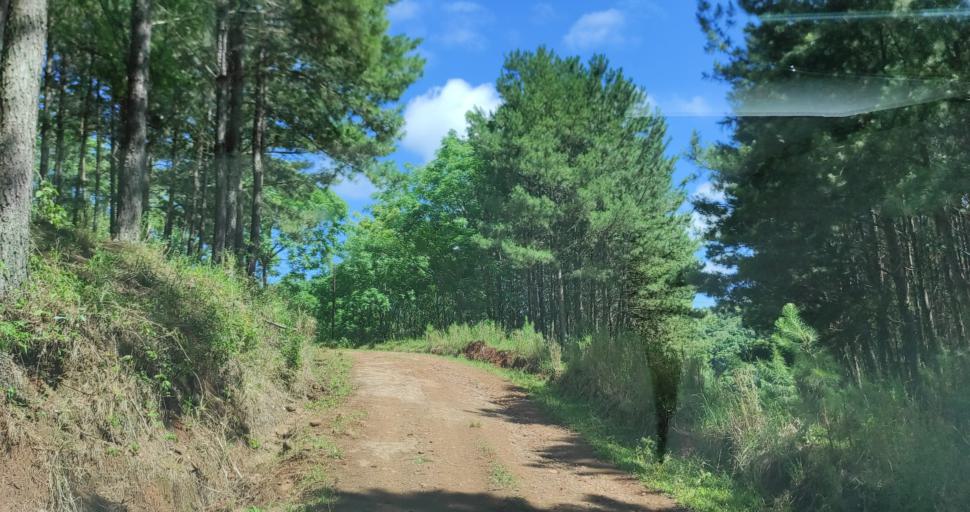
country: AR
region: Misiones
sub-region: Departamento de Veinticinco de Mayo
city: Veinticinco de Mayo
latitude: -27.4167
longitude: -54.7177
